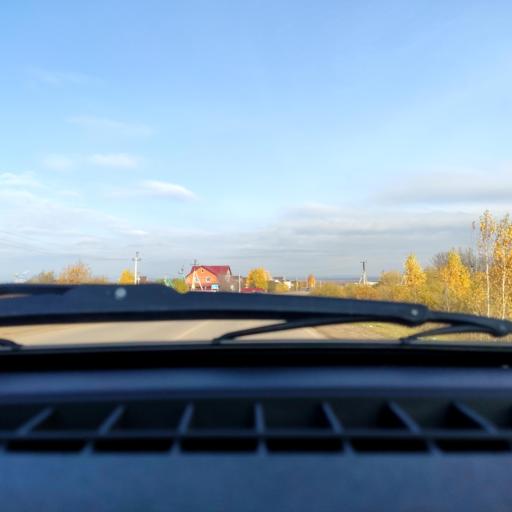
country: RU
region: Bashkortostan
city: Kabakovo
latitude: 54.7088
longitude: 56.1682
